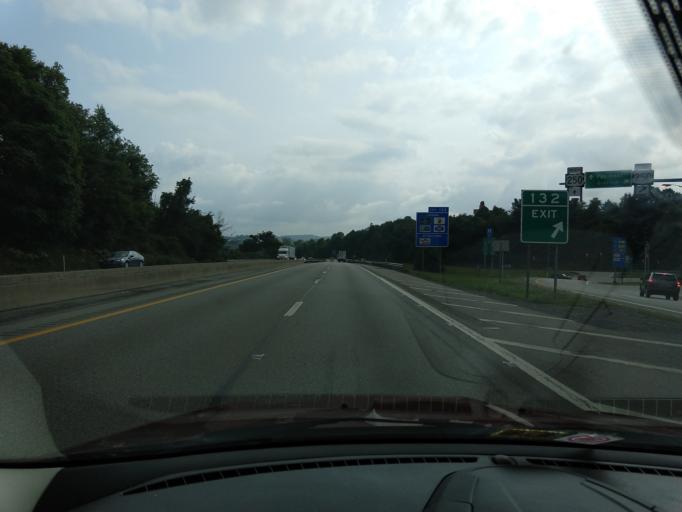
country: US
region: West Virginia
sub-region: Marion County
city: Monongah
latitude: 39.4315
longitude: -80.1892
